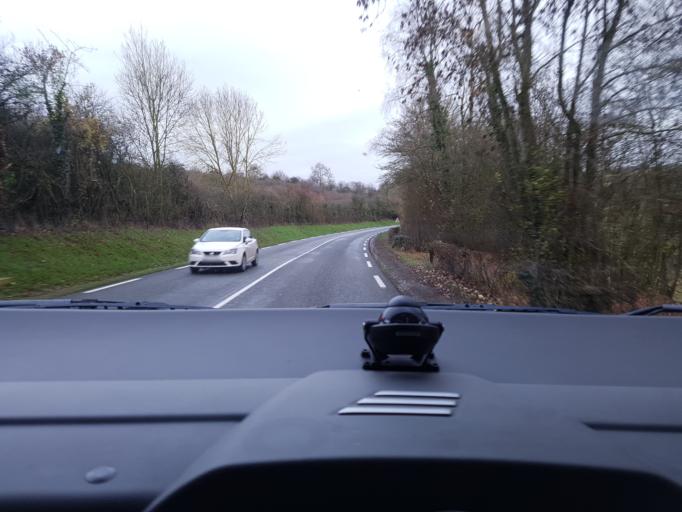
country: FR
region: Picardie
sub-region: Departement de l'Oise
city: Songeons
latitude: 49.5338
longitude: 1.8618
